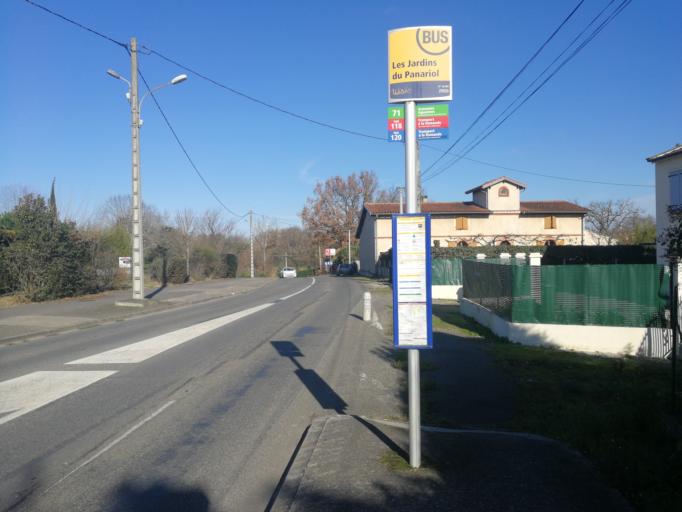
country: FR
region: Midi-Pyrenees
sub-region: Departement de la Haute-Garonne
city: Aussonne
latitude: 43.6790
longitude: 1.3232
